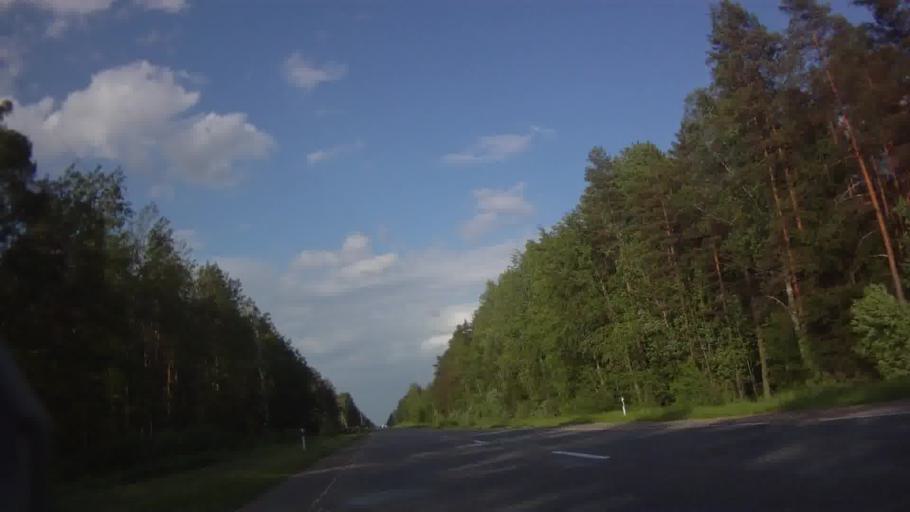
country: LV
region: Incukalns
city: Vangazi
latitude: 57.0976
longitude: 24.5780
